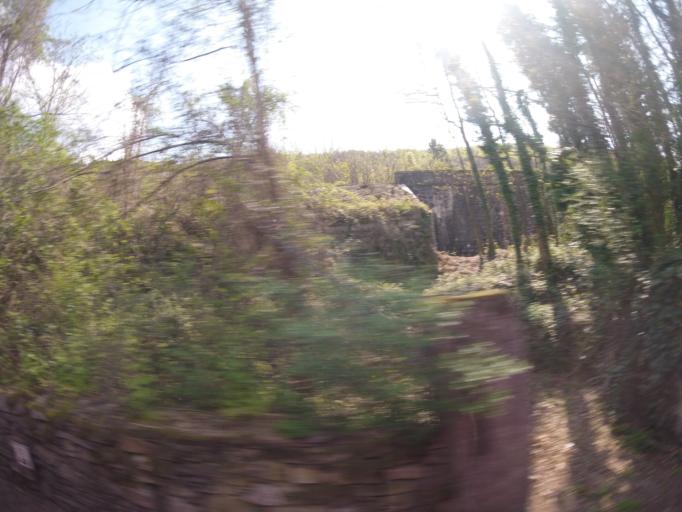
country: IT
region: Piedmont
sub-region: Provincia di Novara
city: Pettenasco
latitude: 45.8412
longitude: 8.4034
